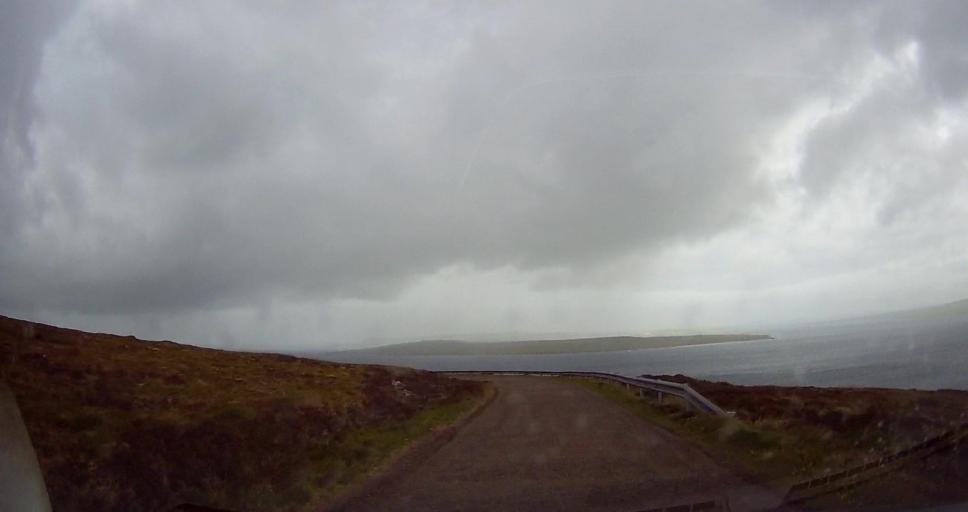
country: GB
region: Scotland
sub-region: Orkney Islands
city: Stromness
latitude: 58.8990
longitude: -3.2742
